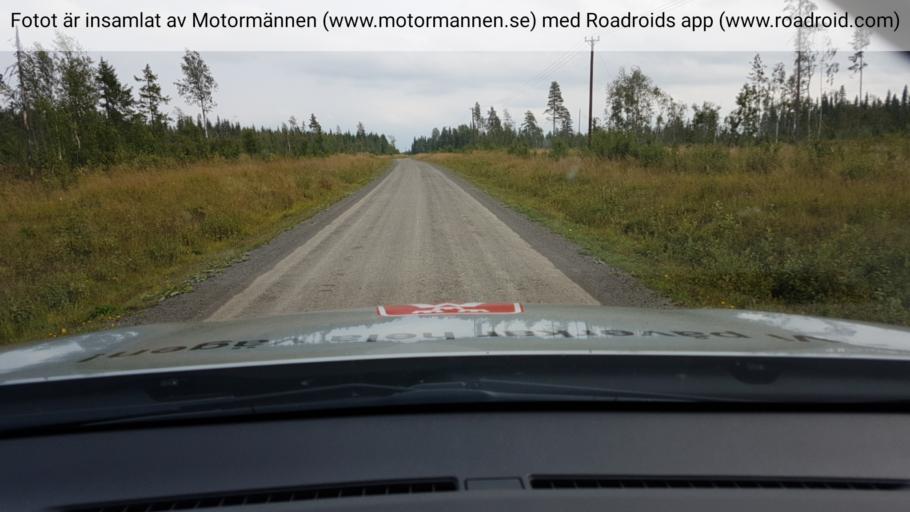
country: SE
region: Jaemtland
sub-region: Stroemsunds Kommun
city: Stroemsund
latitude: 63.7397
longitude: 15.3974
